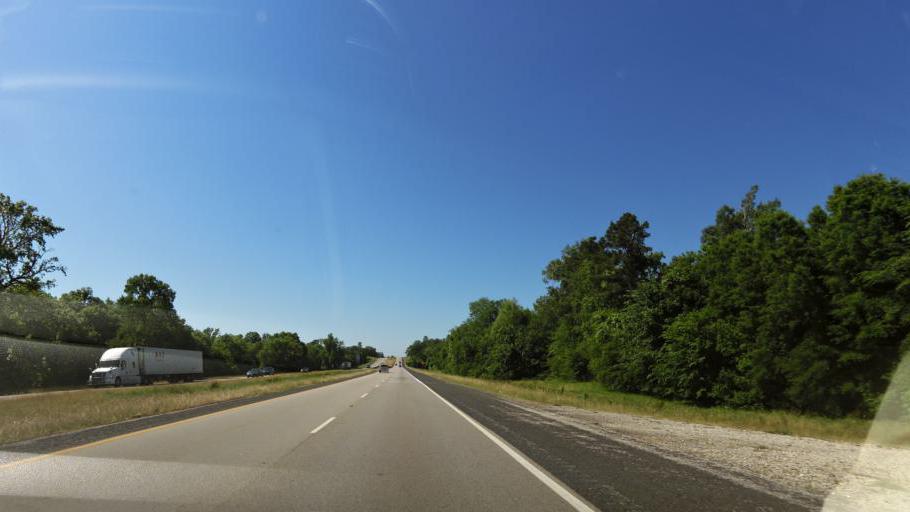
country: US
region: Texas
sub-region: Angelina County
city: Redland
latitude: 31.4515
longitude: -94.7266
